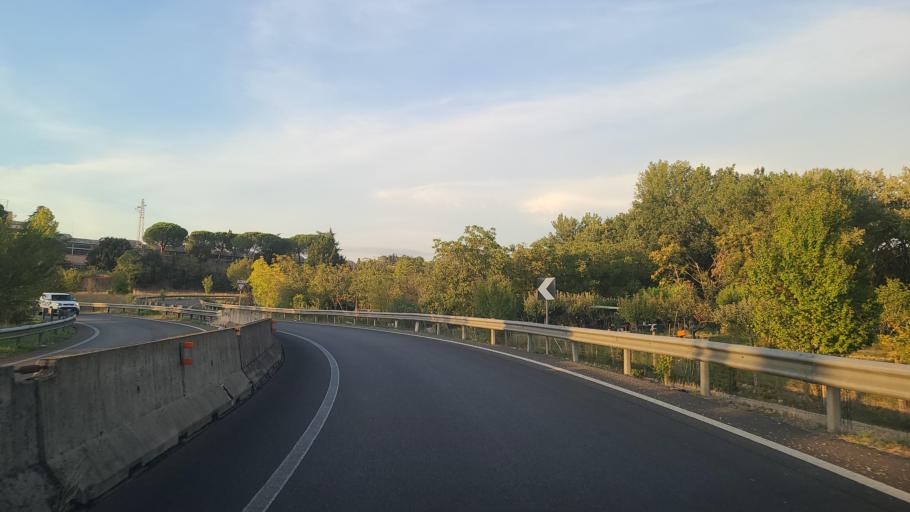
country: IT
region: Tuscany
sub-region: Provincia di Siena
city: Poggibonsi
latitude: 43.4851
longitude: 11.1557
